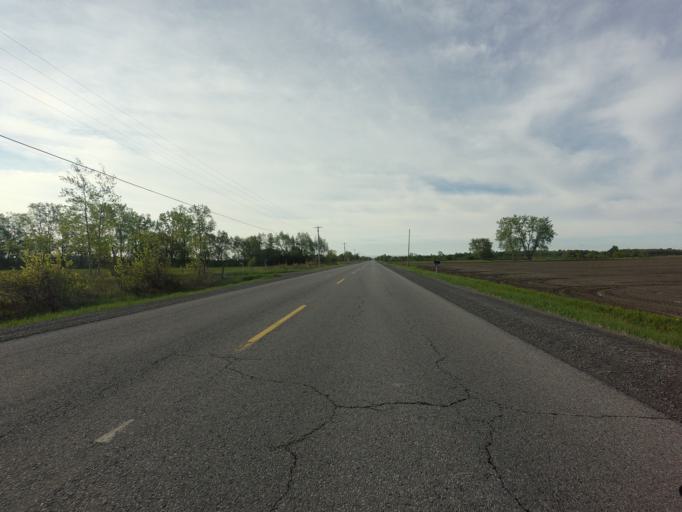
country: CA
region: Ontario
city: Ottawa
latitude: 45.3018
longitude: -75.4546
